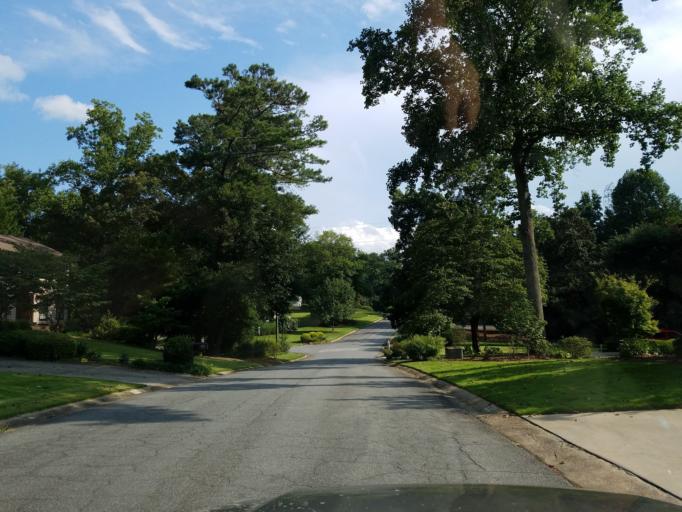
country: US
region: Georgia
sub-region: Fulton County
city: Sandy Springs
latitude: 33.9673
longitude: -84.4439
